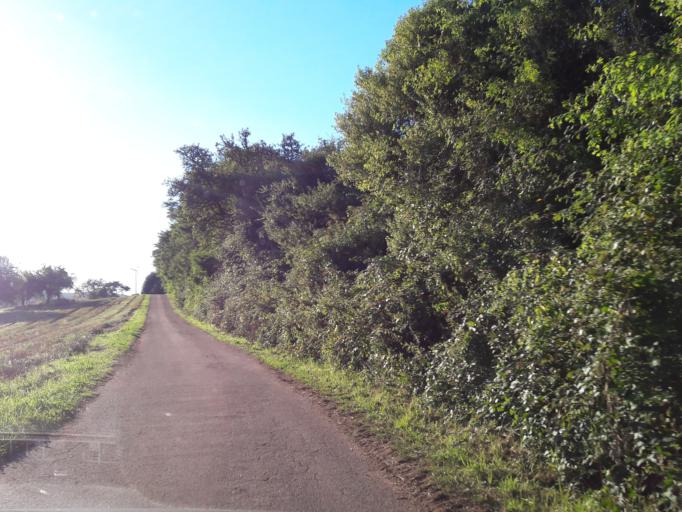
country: DE
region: Rheinland-Pfalz
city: Breitenbach
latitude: 49.4241
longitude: 7.2525
